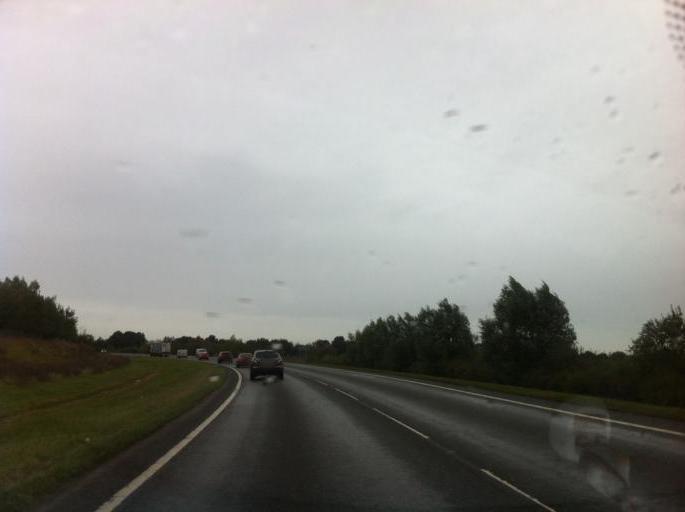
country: GB
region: England
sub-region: Lincolnshire
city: Spalding
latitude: 52.7468
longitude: -0.1224
